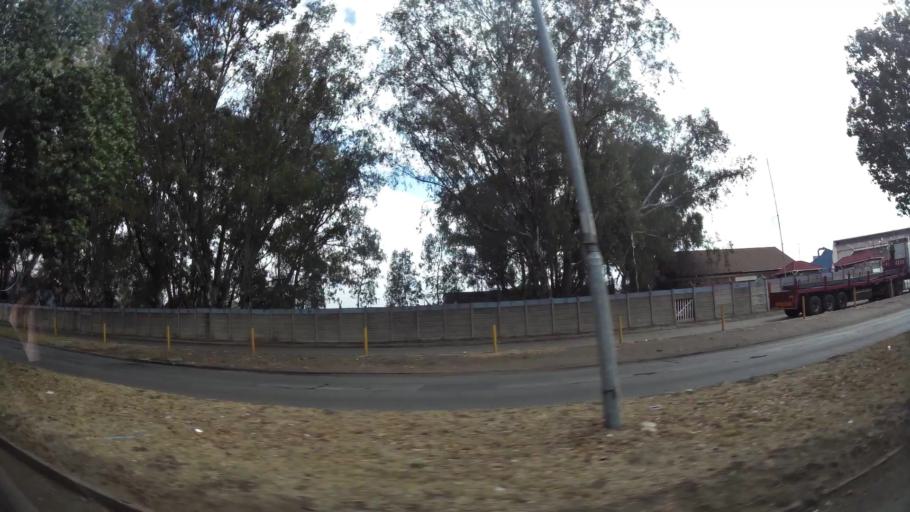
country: ZA
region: Gauteng
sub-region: Sedibeng District Municipality
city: Vereeniging
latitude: -26.6668
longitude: 27.9413
